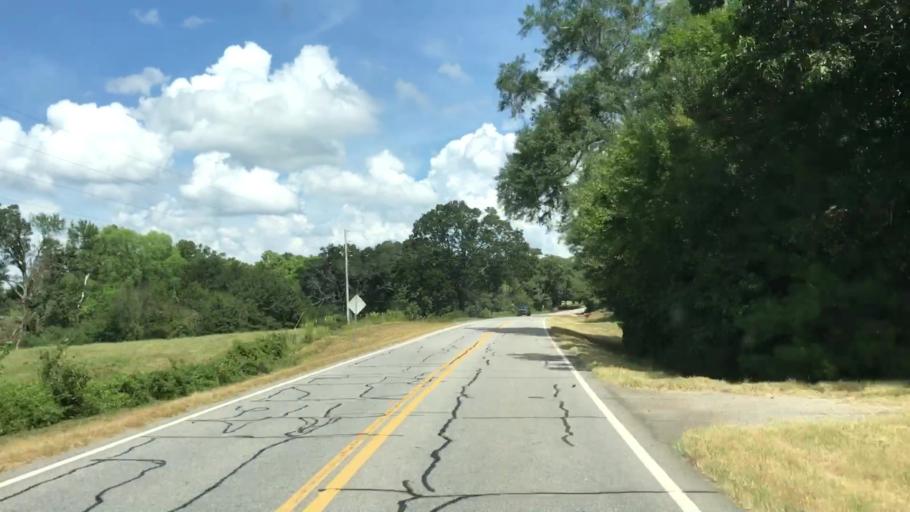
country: US
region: Georgia
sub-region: Oconee County
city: Watkinsville
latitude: 33.7387
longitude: -83.3035
